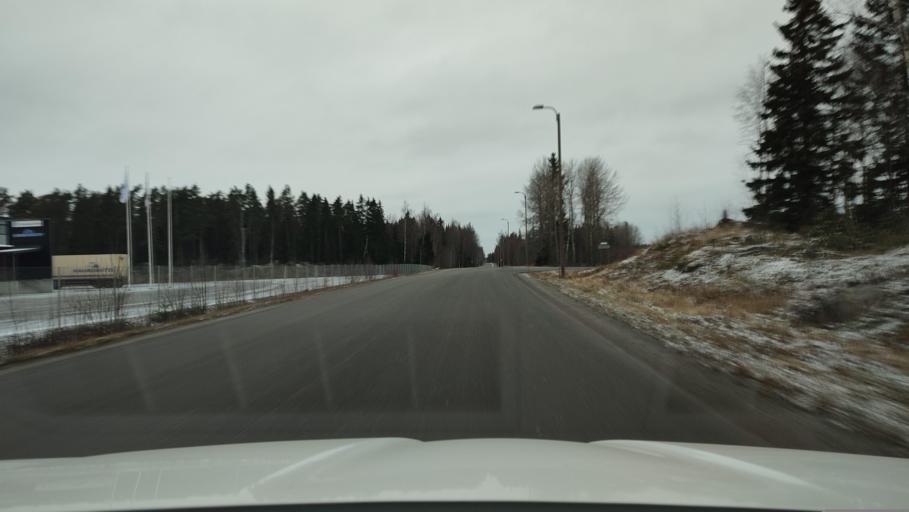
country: FI
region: Ostrobothnia
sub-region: Vaasa
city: Ristinummi
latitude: 63.0387
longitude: 21.7805
